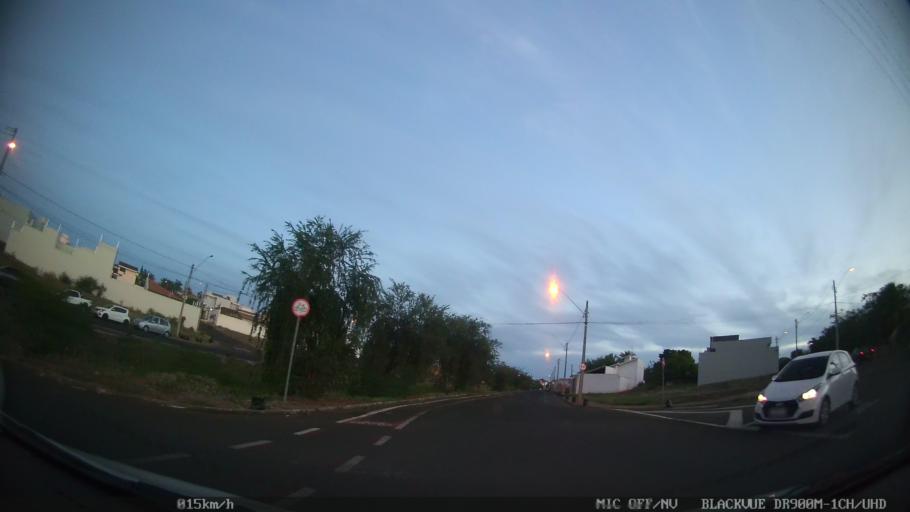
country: BR
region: Sao Paulo
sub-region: Catanduva
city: Catanduva
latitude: -21.1420
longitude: -48.9902
